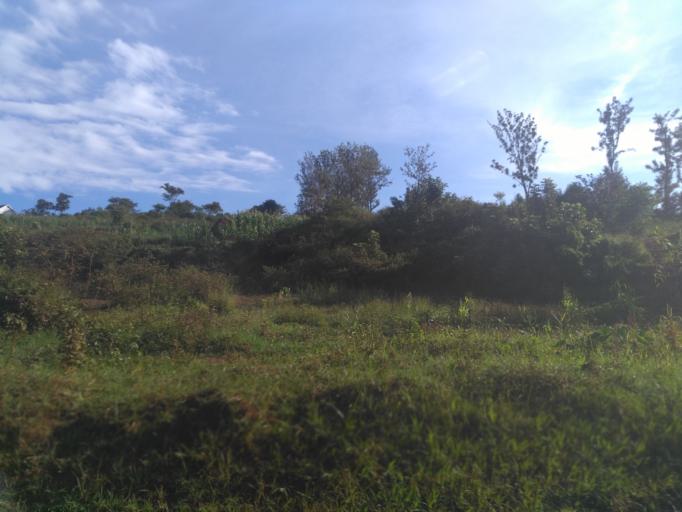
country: UG
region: Eastern Region
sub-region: Jinja District
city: Jinja
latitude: 0.4661
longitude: 33.1757
